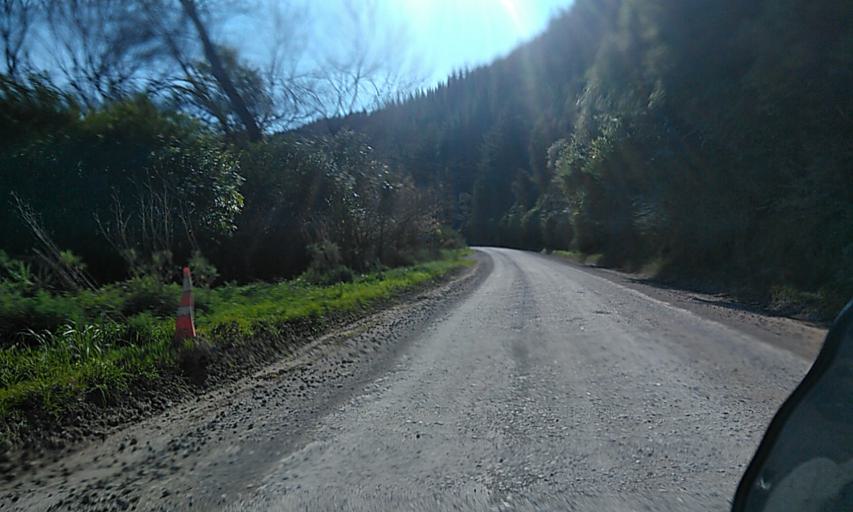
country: NZ
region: Gisborne
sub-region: Gisborne District
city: Gisborne
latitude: -38.5373
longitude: 178.0372
